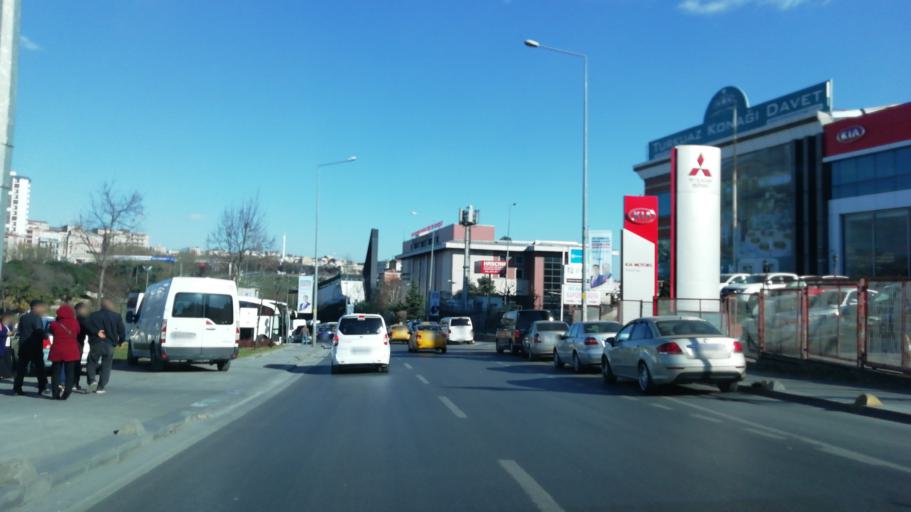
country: TR
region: Istanbul
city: Bagcilar
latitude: 41.0532
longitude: 28.8626
